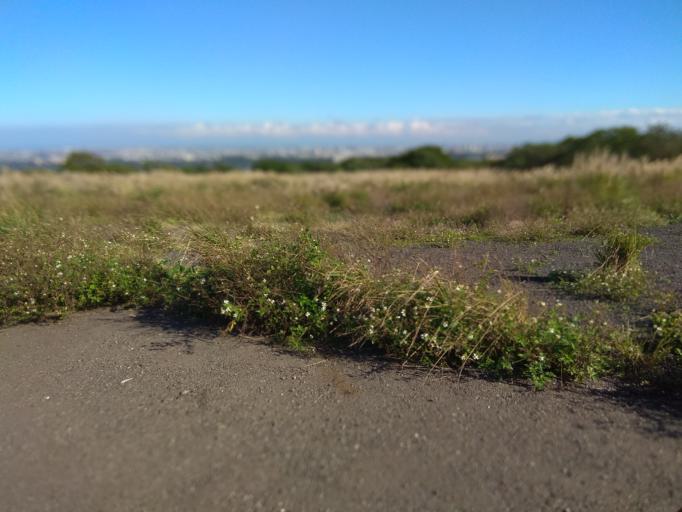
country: TW
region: Taiwan
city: Daxi
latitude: 24.8905
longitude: 121.1487
